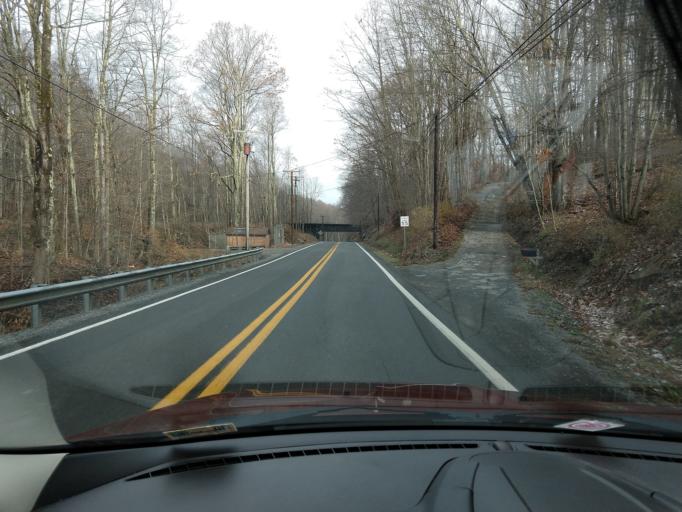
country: US
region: West Virginia
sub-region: Greenbrier County
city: Rainelle
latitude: 38.0651
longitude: -80.7085
